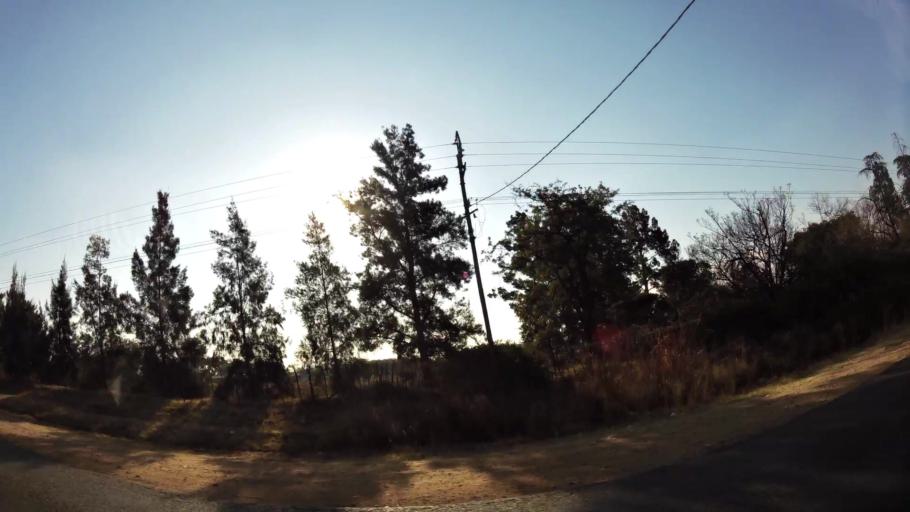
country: ZA
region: Gauteng
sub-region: West Rand District Municipality
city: Muldersdriseloop
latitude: -26.0171
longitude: 27.8845
